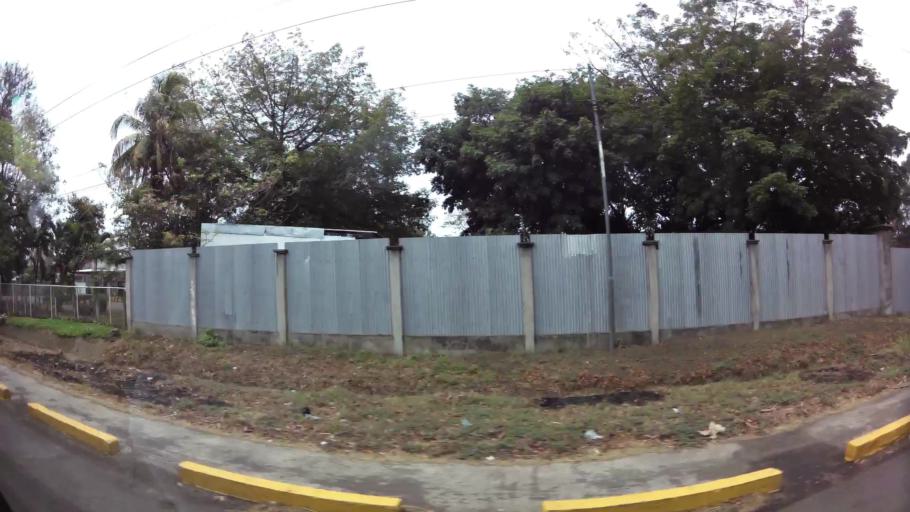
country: NI
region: Chinandega
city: Chinandega
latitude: 12.6211
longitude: -87.1162
